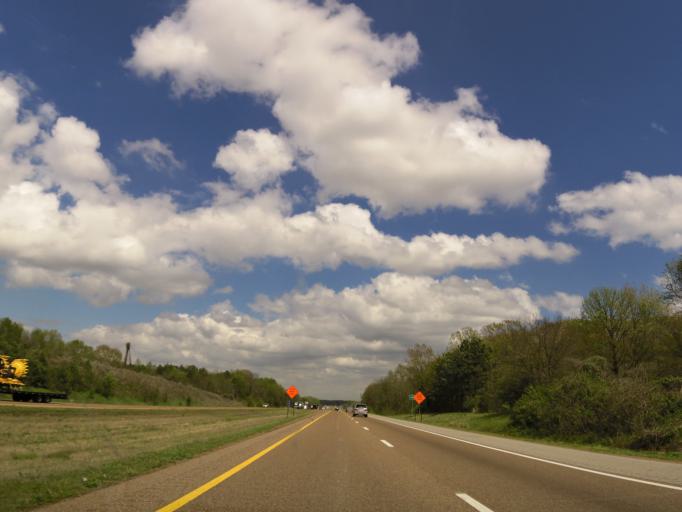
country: US
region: Tennessee
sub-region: Shelby County
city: Arlington
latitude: 35.2788
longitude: -89.6330
